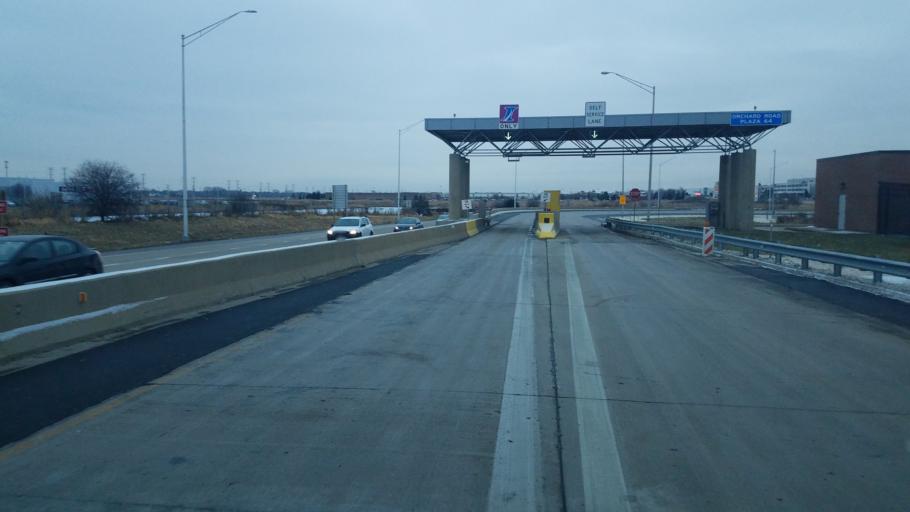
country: US
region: Illinois
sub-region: Kane County
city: North Aurora
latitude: 41.7967
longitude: -88.3746
